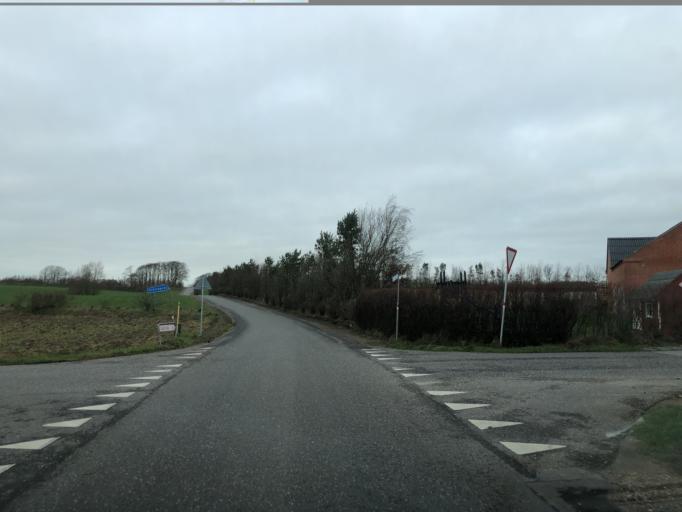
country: DK
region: Central Jutland
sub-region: Viborg Kommune
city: Stoholm
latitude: 56.4492
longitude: 9.1067
